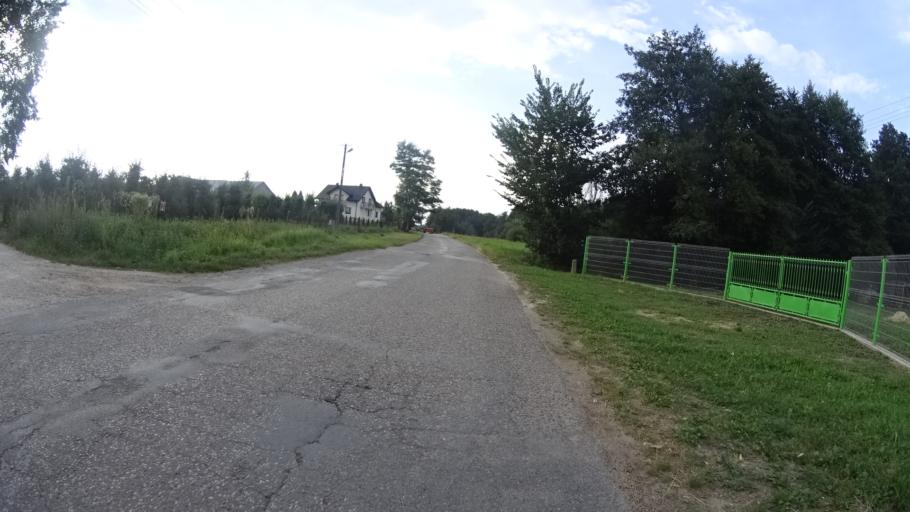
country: PL
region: Masovian Voivodeship
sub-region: Powiat grojecki
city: Mogielnica
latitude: 51.6738
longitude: 20.7391
